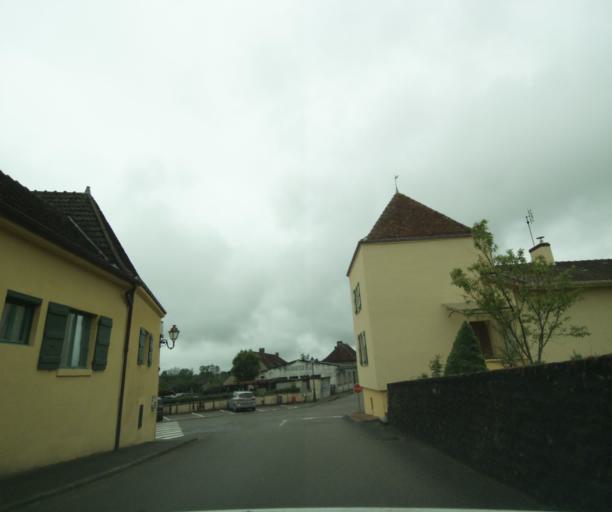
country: FR
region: Bourgogne
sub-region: Departement de Saone-et-Loire
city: Charolles
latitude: 46.4410
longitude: 4.3385
